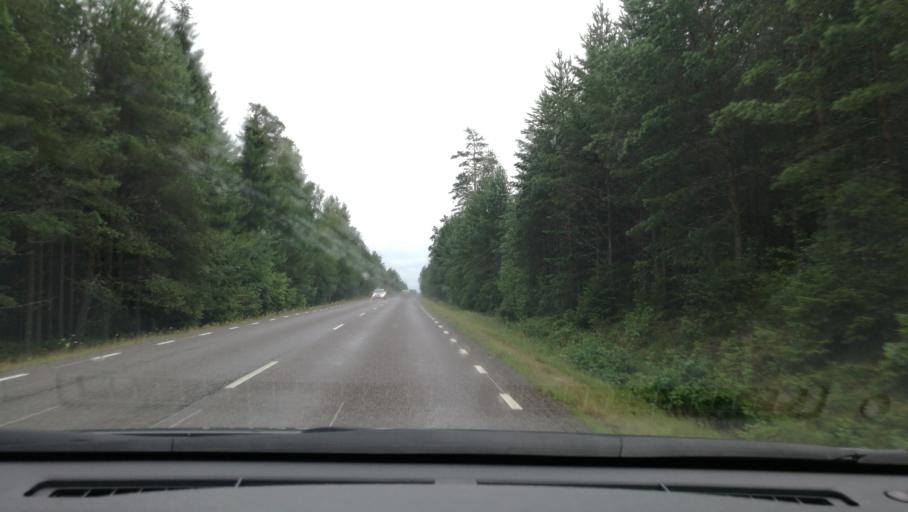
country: SE
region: OEstergoetland
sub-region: Norrkopings Kommun
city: Svartinge
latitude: 58.7680
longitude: 15.9708
